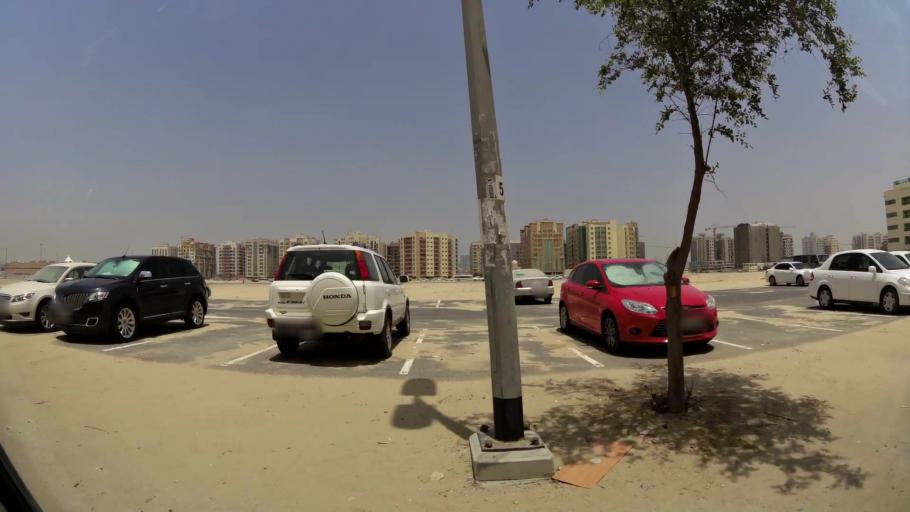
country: AE
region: Ash Shariqah
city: Sharjah
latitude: 25.2840
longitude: 55.4048
